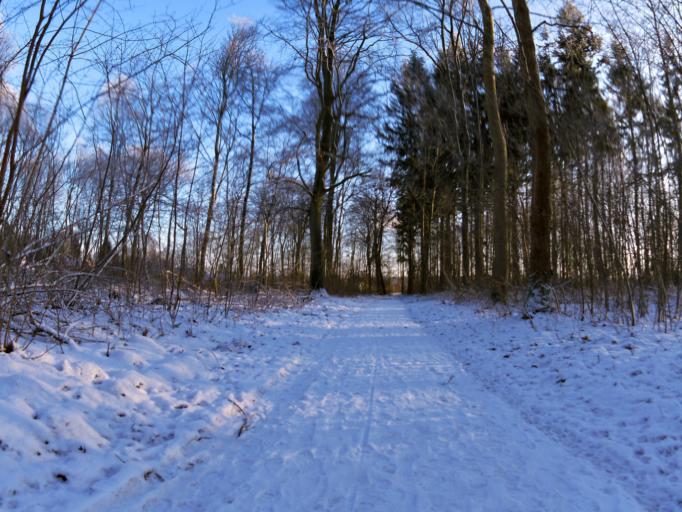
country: DK
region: Central Jutland
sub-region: Arhus Kommune
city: Stavtrup
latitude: 56.1515
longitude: 10.0816
